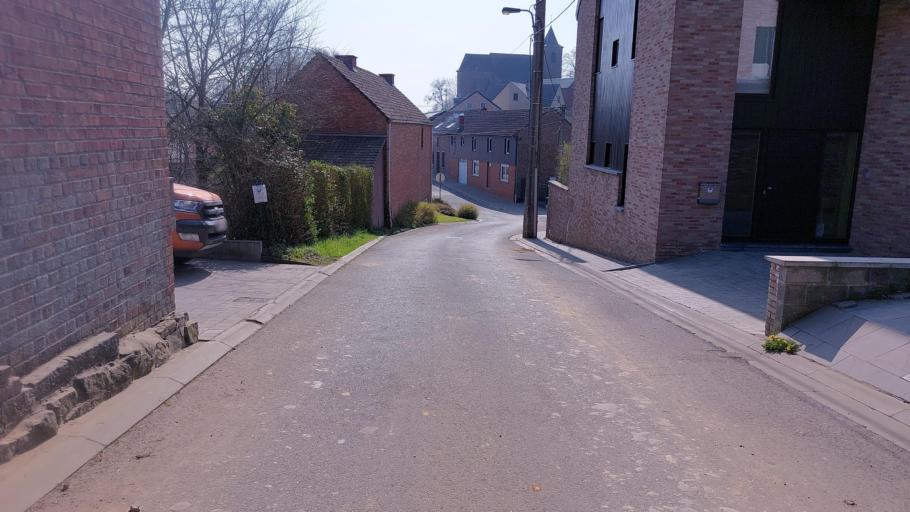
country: BE
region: Wallonia
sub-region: Province du Hainaut
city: Roeulx
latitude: 50.4969
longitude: 4.0644
